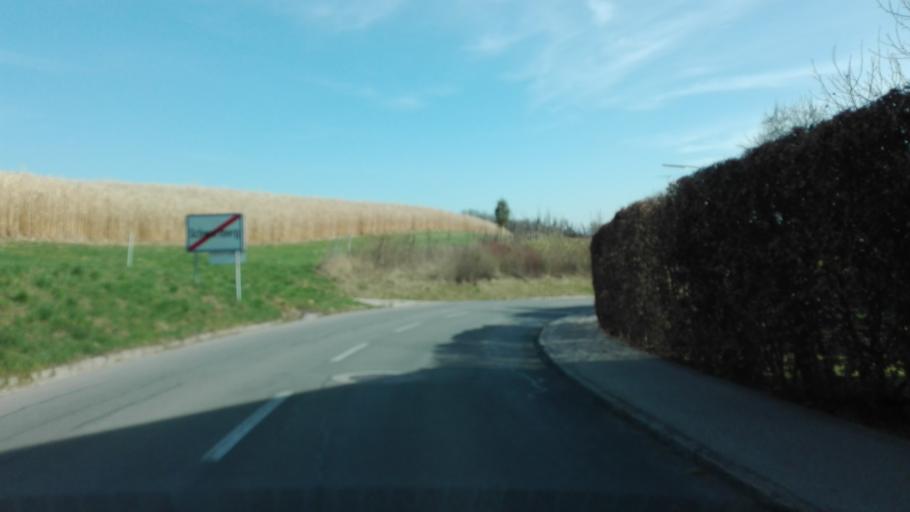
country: AT
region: Upper Austria
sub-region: Politischer Bezirk Perg
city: Perg
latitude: 48.2636
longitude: 14.5882
